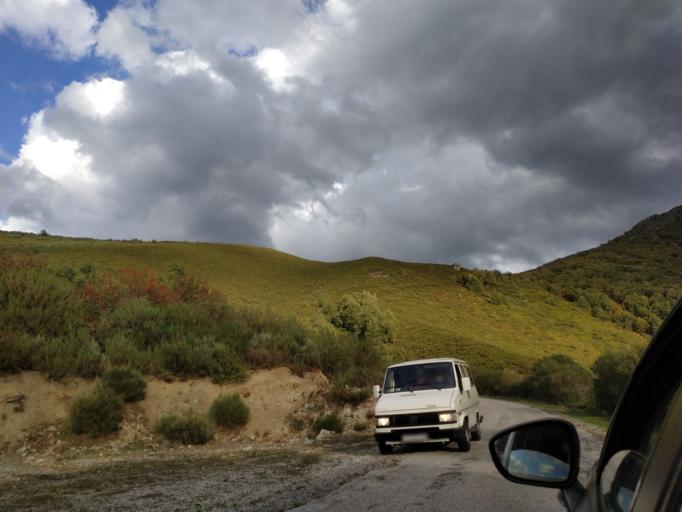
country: ES
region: Castille and Leon
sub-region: Provincia de Leon
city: Candin
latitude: 42.8675
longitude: -6.8353
